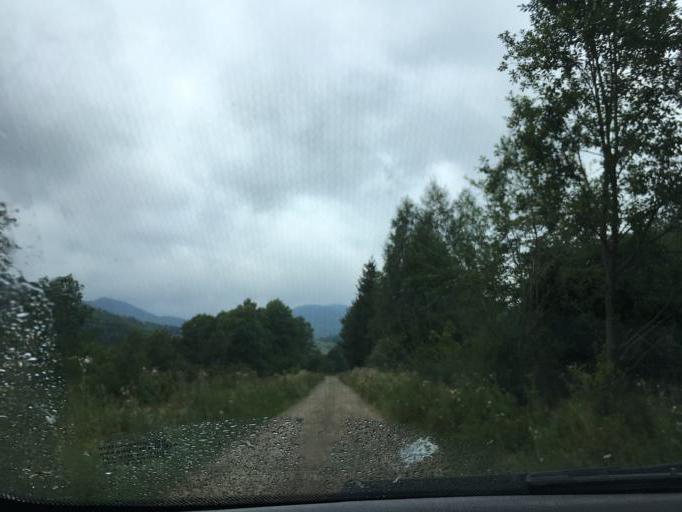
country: PL
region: Subcarpathian Voivodeship
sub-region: Powiat bieszczadzki
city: Lutowiska
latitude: 49.1627
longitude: 22.6248
